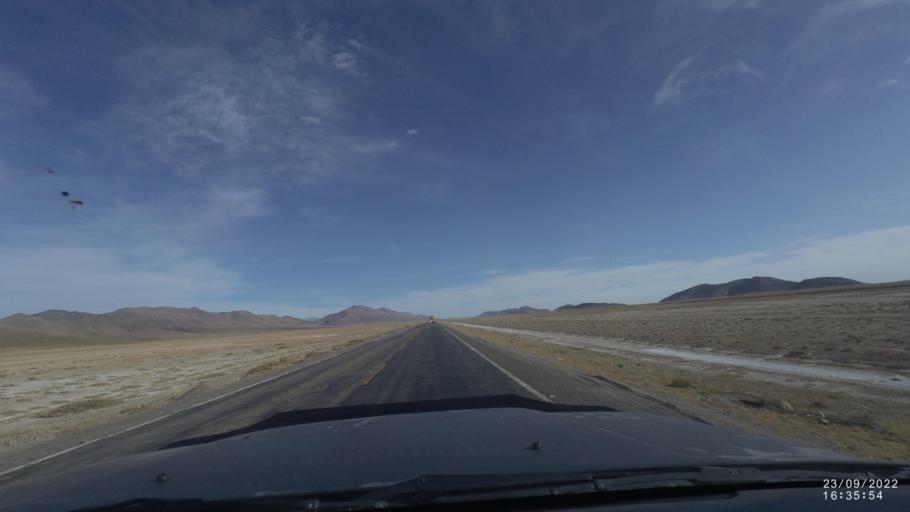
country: BO
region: Oruro
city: Machacamarca
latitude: -18.2116
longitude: -67.0096
